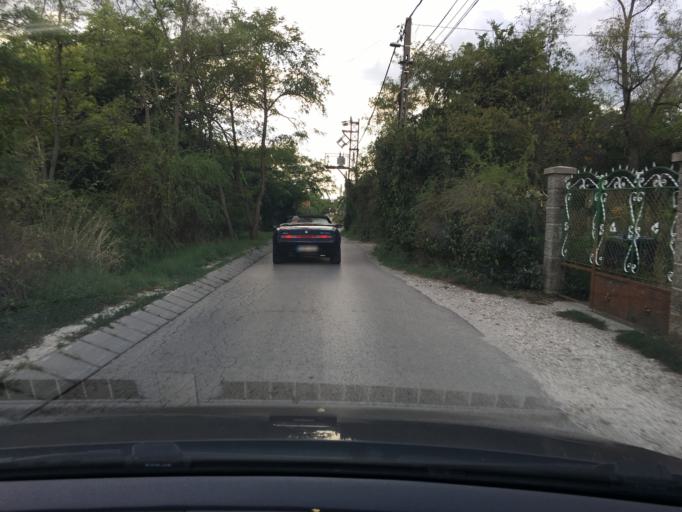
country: HU
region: Pest
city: Szada
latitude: 47.6423
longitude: 19.3083
